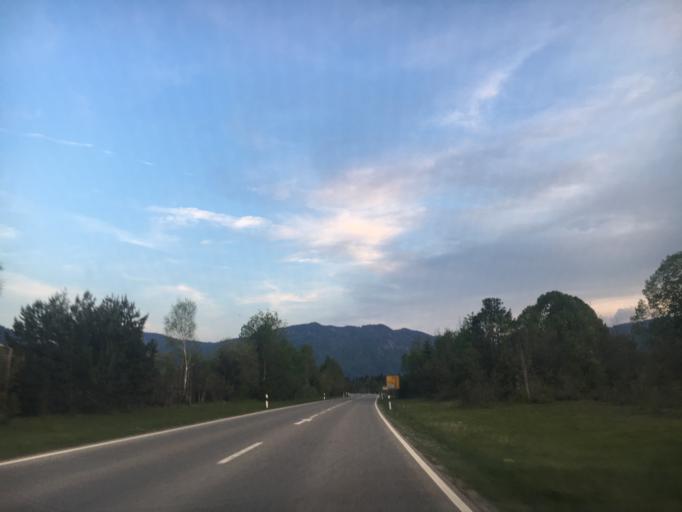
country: DE
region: Bavaria
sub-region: Upper Bavaria
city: Lenggries
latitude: 47.6642
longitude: 11.5832
